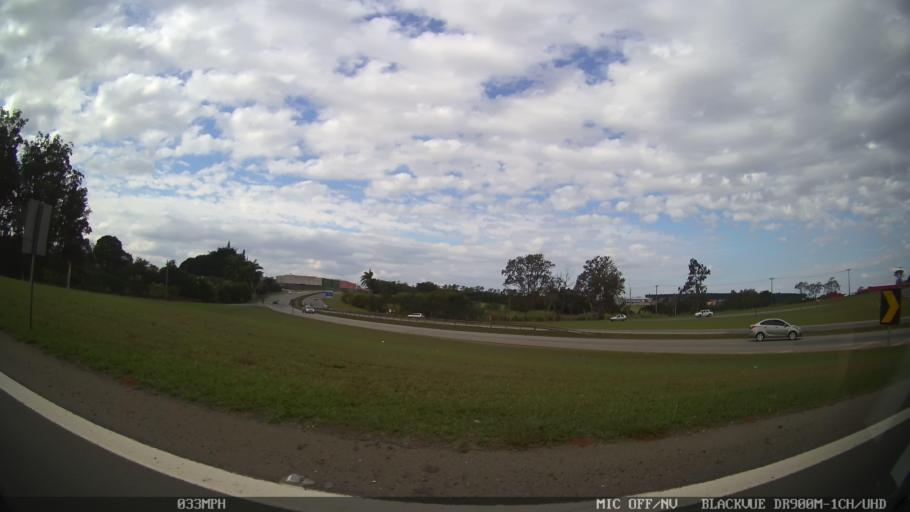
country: BR
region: Sao Paulo
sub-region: Limeira
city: Limeira
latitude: -22.5442
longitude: -47.3754
